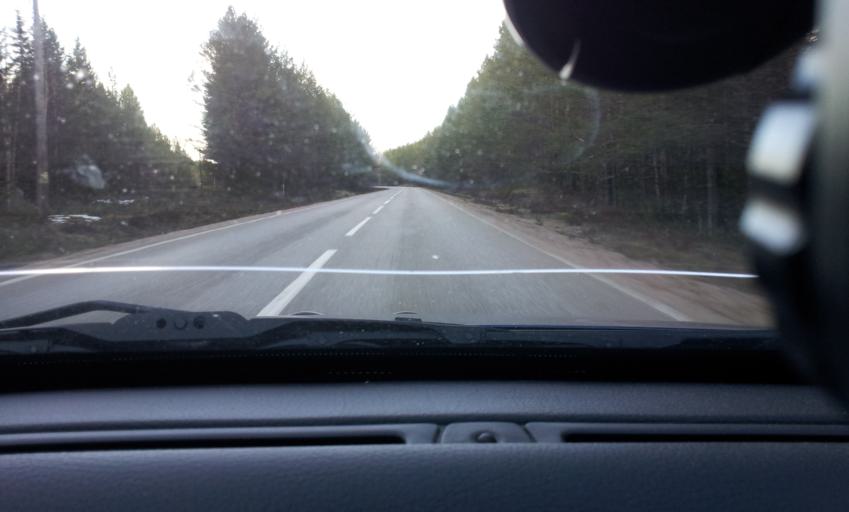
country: SE
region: Vaesternorrland
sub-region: Ange Kommun
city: Ange
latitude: 62.0852
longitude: 15.0948
